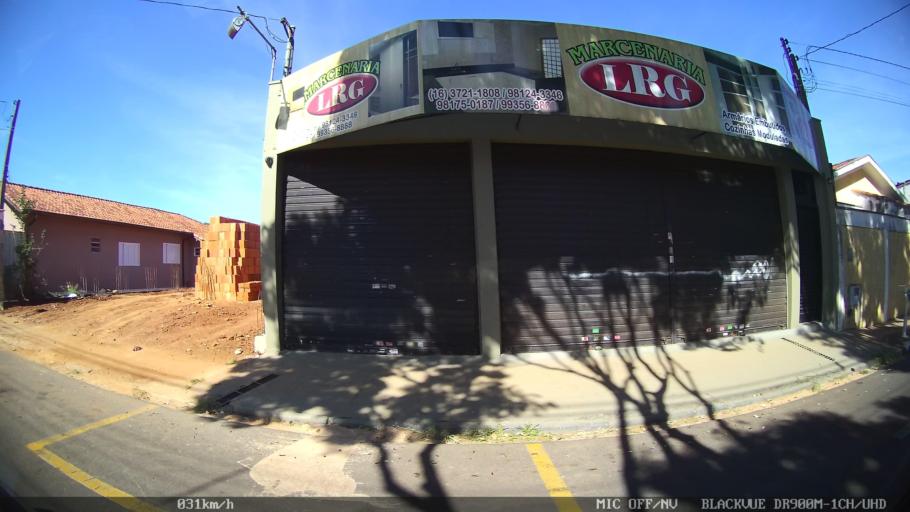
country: BR
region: Sao Paulo
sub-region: Franca
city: Franca
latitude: -20.5440
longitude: -47.3840
